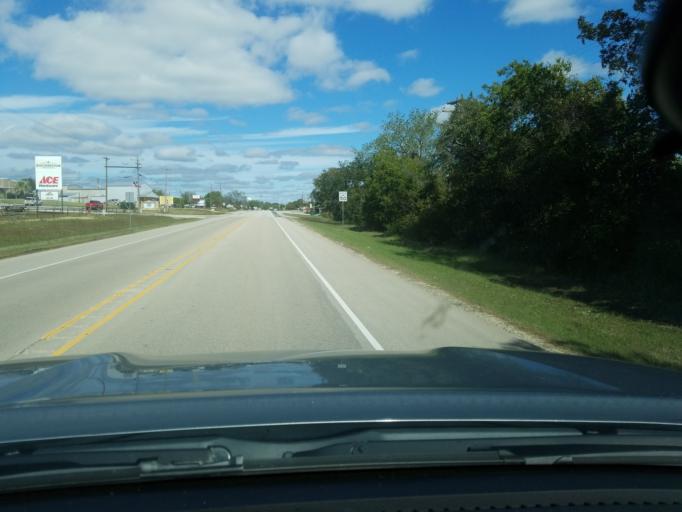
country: US
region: Texas
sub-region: Hamilton County
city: Hamilton
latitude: 31.6892
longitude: -98.1302
